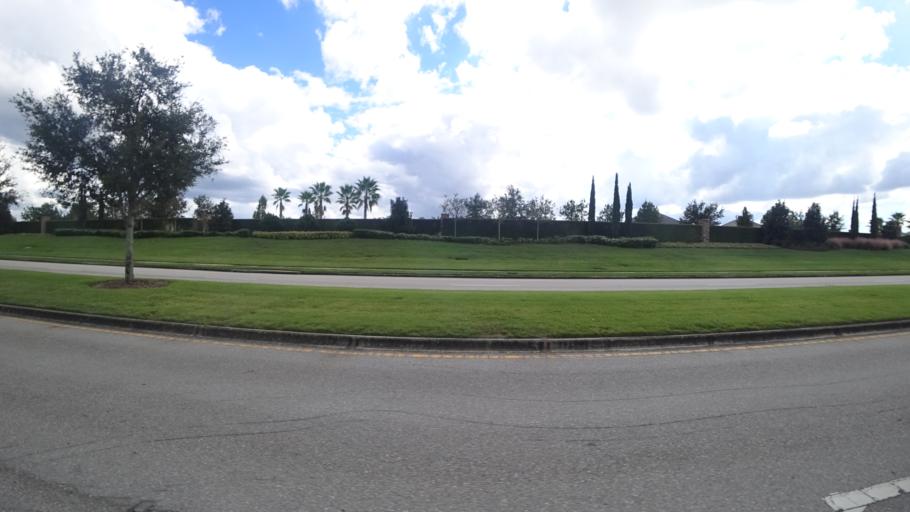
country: US
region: Florida
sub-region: Sarasota County
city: The Meadows
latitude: 27.4025
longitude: -82.3776
